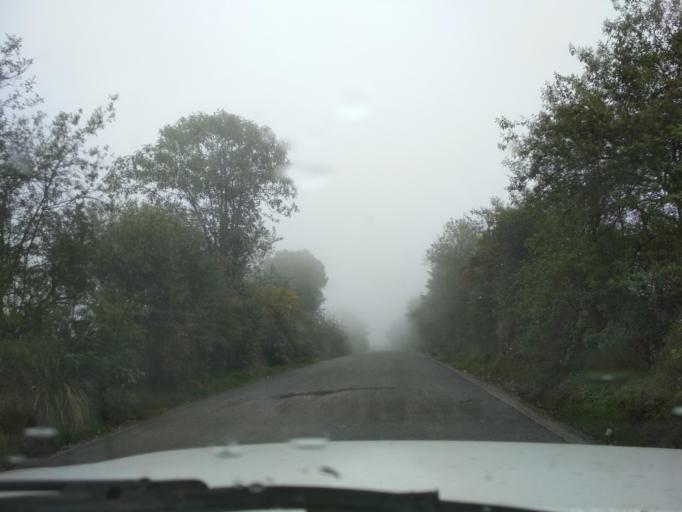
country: MX
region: Veracruz
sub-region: Mariano Escobedo
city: Loma Grande
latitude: 18.9350
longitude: -97.2213
